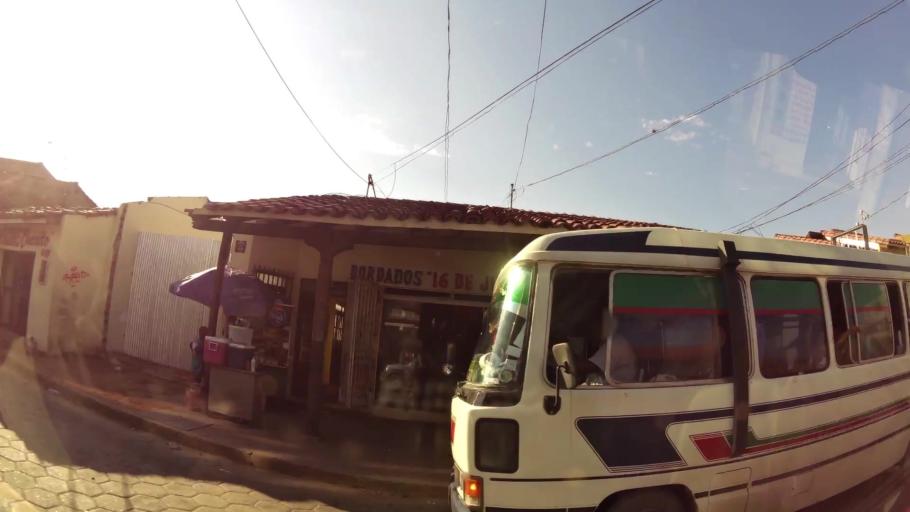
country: BO
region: Santa Cruz
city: Santa Cruz de la Sierra
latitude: -17.7842
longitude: -63.1739
